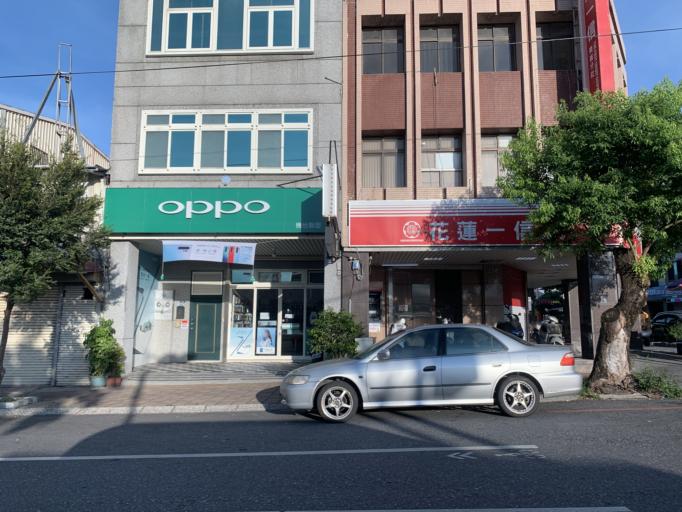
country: TW
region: Taiwan
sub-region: Hualien
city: Hualian
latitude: 23.9955
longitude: 121.6294
